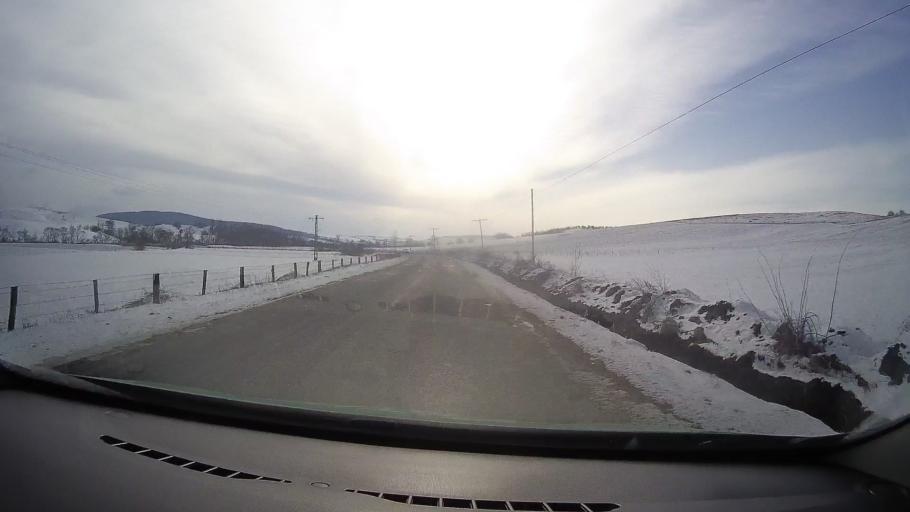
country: RO
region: Sibiu
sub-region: Oras Agnita
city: Ruja
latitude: 46.0101
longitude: 24.6839
